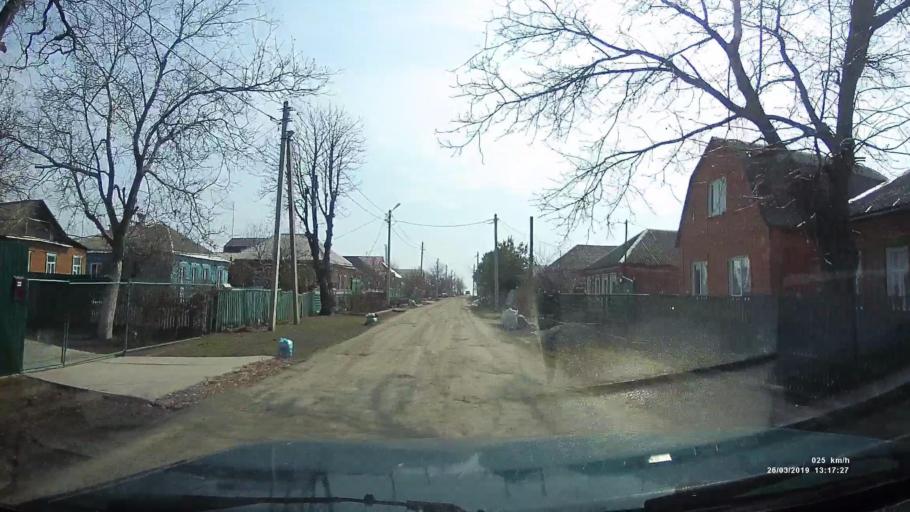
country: RU
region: Rostov
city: Novobessergenovka
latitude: 47.1715
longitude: 38.7671
